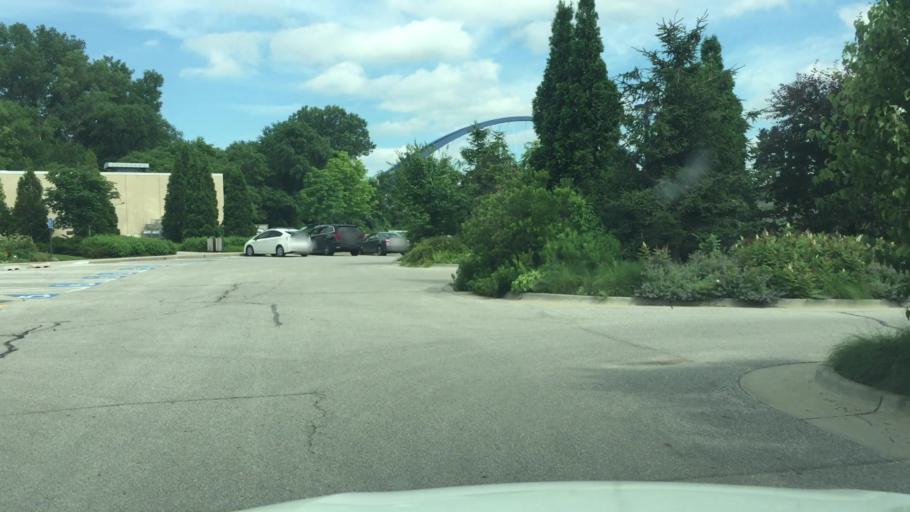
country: US
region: Iowa
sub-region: Polk County
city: Des Moines
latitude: 41.5965
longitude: -93.6147
